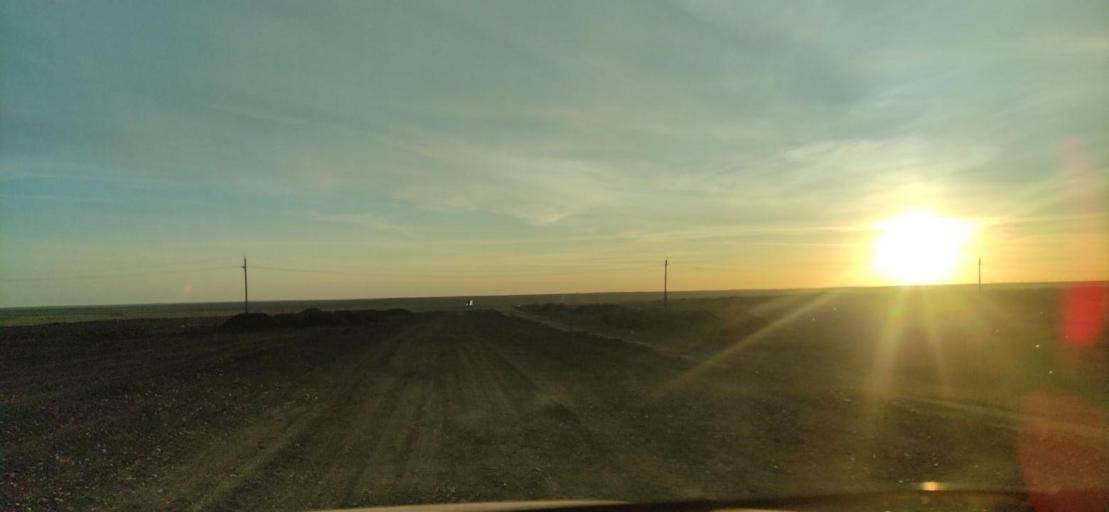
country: KZ
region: Qaraghandy
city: Saryshaghan
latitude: 46.0077
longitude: 73.5858
